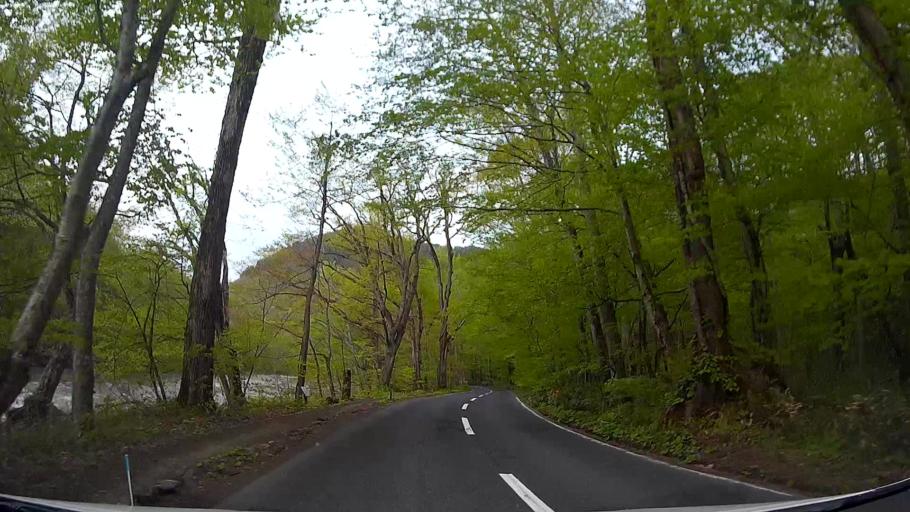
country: JP
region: Aomori
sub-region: Aomori Shi
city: Furudate
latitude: 40.5681
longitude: 140.9774
